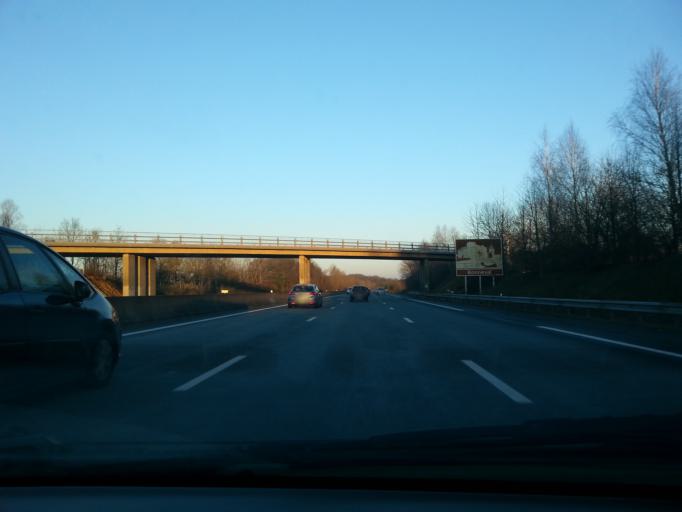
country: FR
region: Centre
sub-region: Departement d'Eure-et-Loir
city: Authon-du-Perche
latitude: 48.2201
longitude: 0.9615
